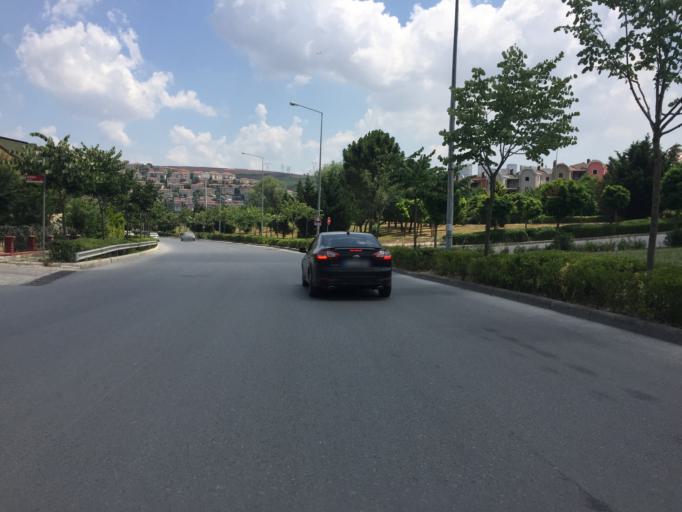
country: TR
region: Istanbul
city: Esenyurt
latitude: 41.0841
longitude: 28.6690
